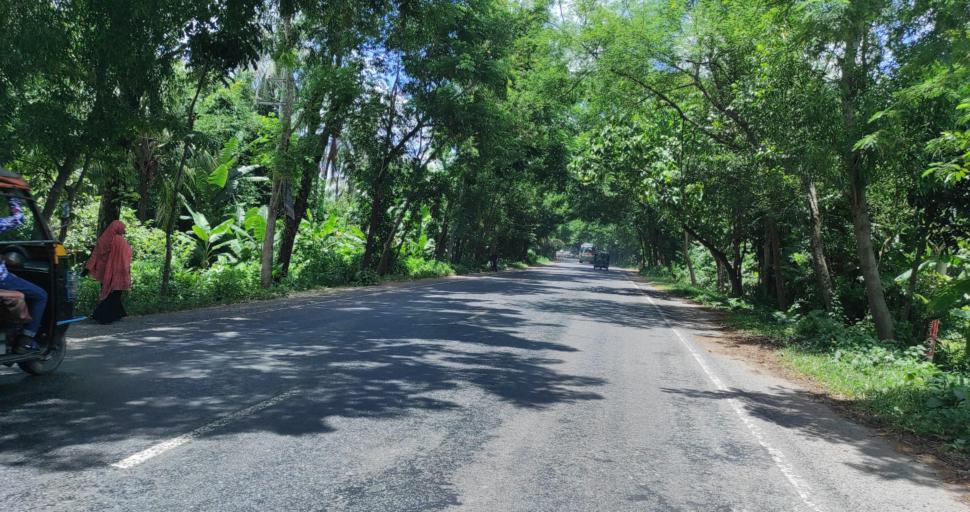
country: BD
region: Barisal
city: Gaurnadi
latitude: 22.8341
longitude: 90.2544
